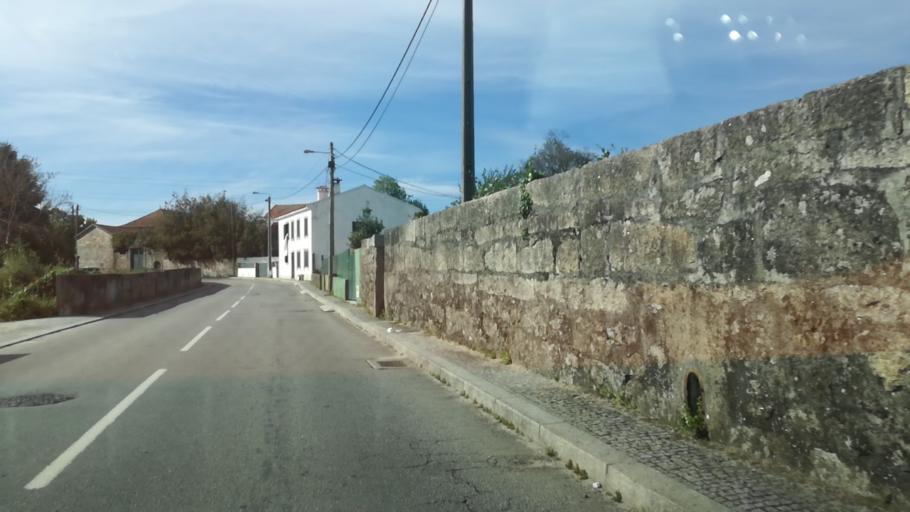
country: PT
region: Porto
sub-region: Maia
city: Nogueira
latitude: 41.2322
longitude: -8.5872
